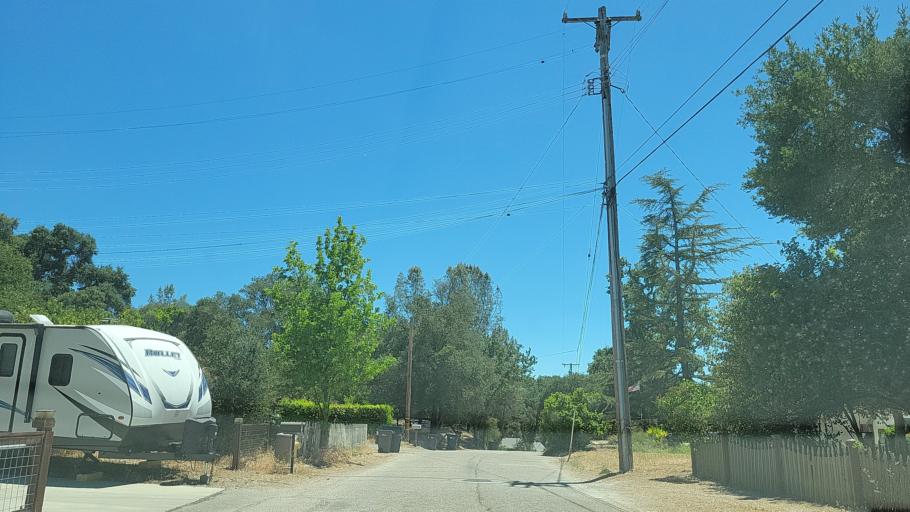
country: US
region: California
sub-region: San Luis Obispo County
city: Atascadero
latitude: 35.4782
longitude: -120.6624
